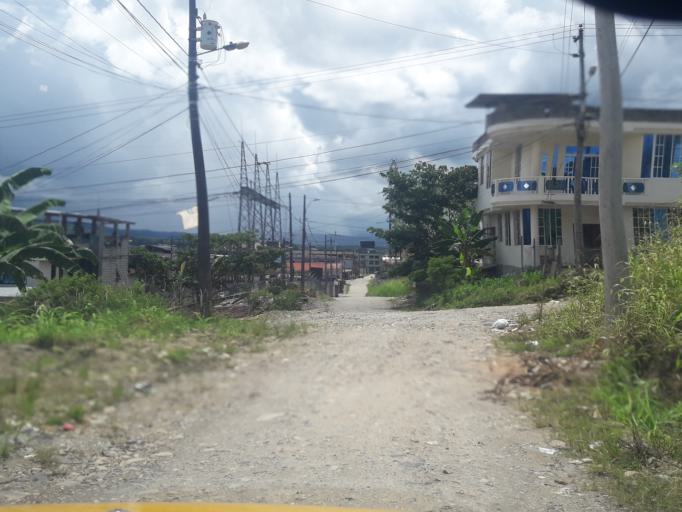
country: EC
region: Napo
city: Tena
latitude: -1.0083
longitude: -77.8108
